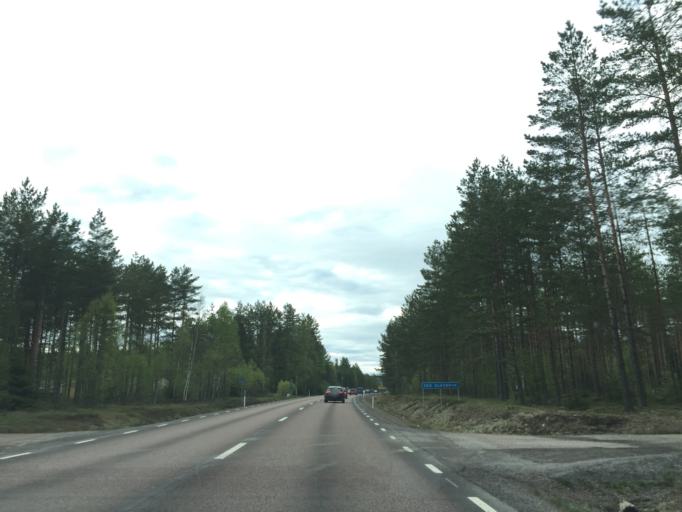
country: SE
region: Vaermland
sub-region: Eda Kommun
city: Charlottenberg
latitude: 59.9085
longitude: 12.2752
